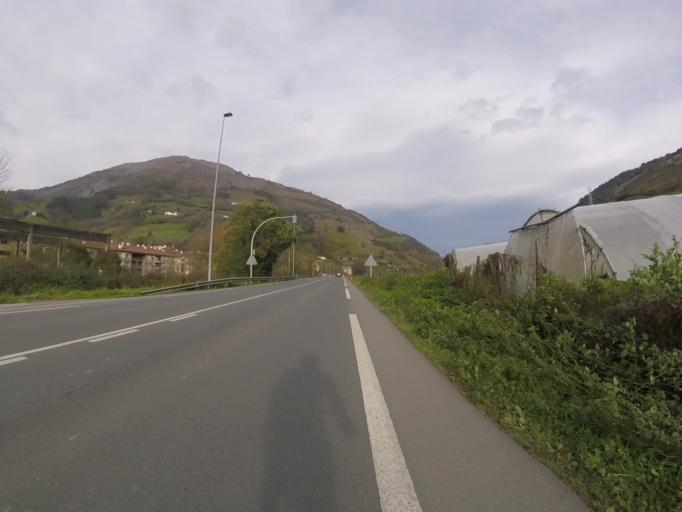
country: ES
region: Basque Country
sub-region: Provincia de Guipuzcoa
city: Azpeitia
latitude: 43.1854
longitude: -2.2604
